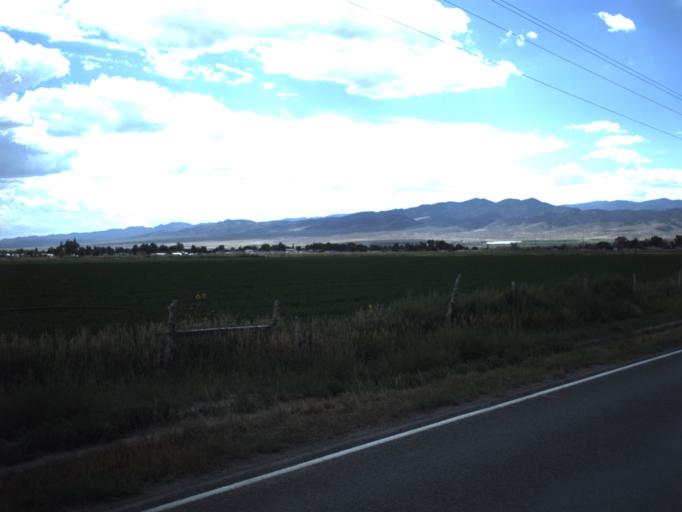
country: US
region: Utah
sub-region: Sanpete County
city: Gunnison
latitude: 39.1418
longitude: -111.8062
